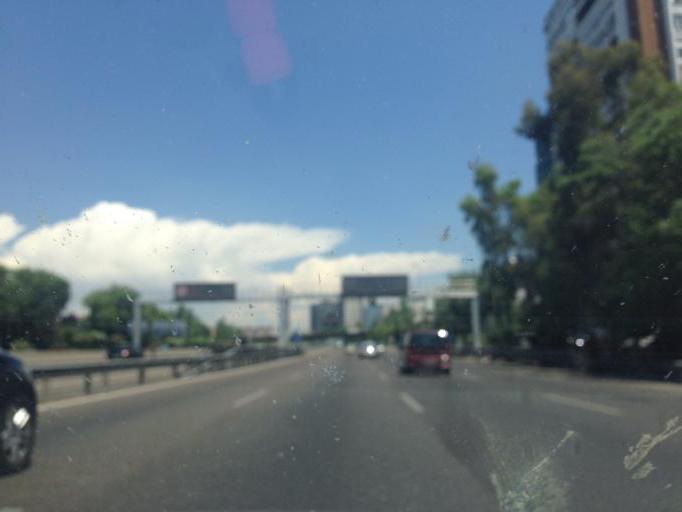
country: ES
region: Madrid
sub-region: Provincia de Madrid
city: Salamanca
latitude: 40.4362
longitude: -3.6594
